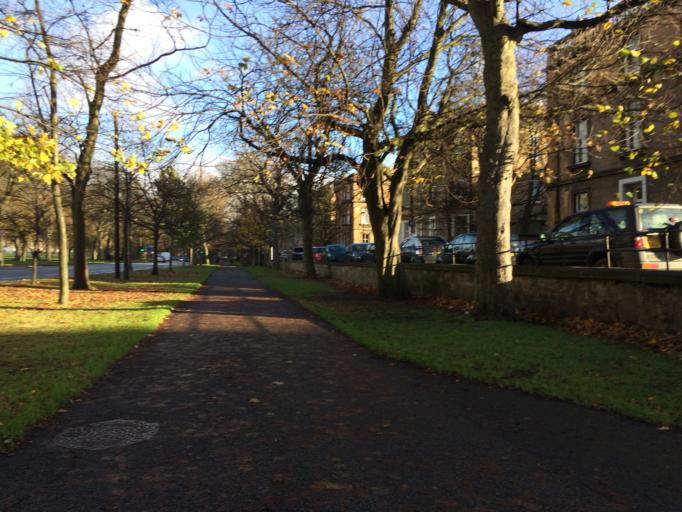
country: GB
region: Scotland
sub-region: Edinburgh
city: Edinburgh
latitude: 55.9395
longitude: -3.1893
